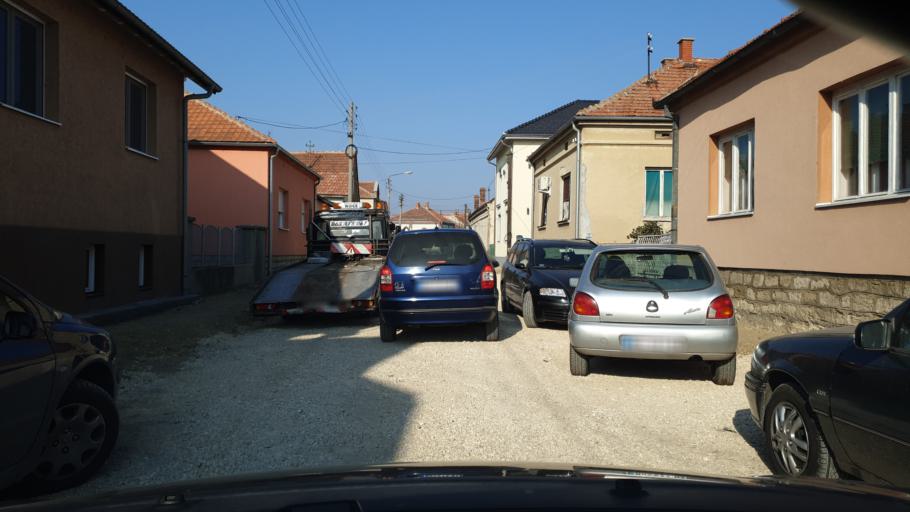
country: RS
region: Central Serbia
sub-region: Borski Okrug
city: Negotin
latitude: 44.2260
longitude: 22.5273
